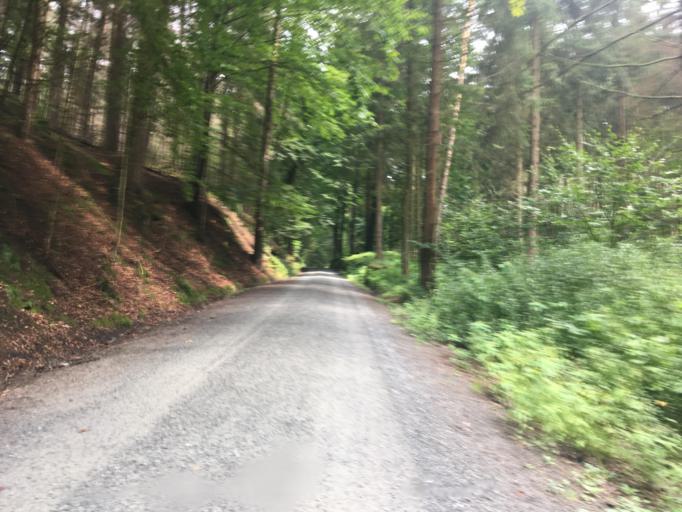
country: DE
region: Saxony
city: Bad Schandau
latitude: 50.9200
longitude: 14.1983
